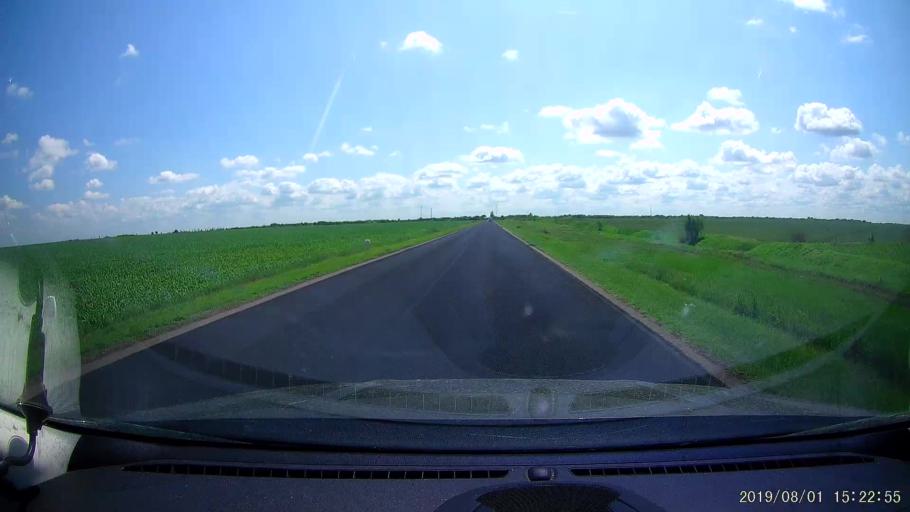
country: RO
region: Braila
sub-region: Comuna Viziru
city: Lanurile
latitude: 45.0476
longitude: 27.7687
